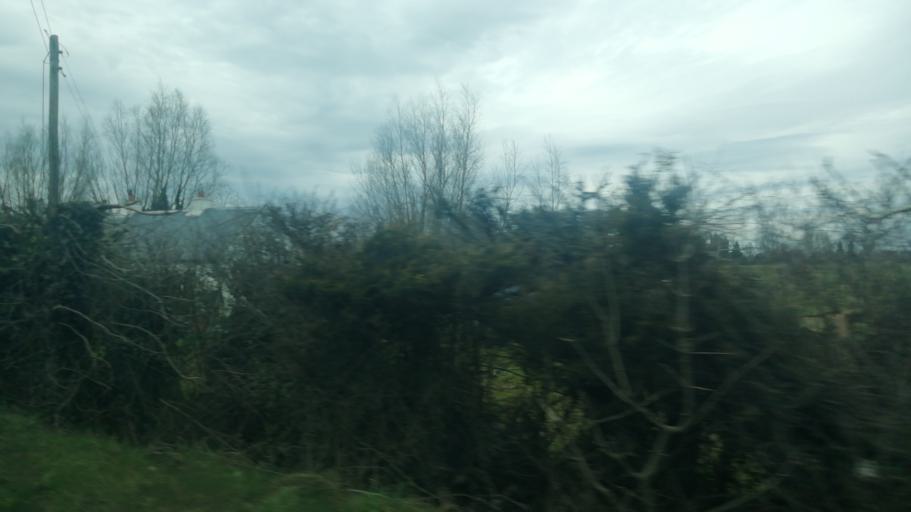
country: IE
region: Leinster
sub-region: Kildare
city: Prosperous
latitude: 53.2857
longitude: -6.8161
